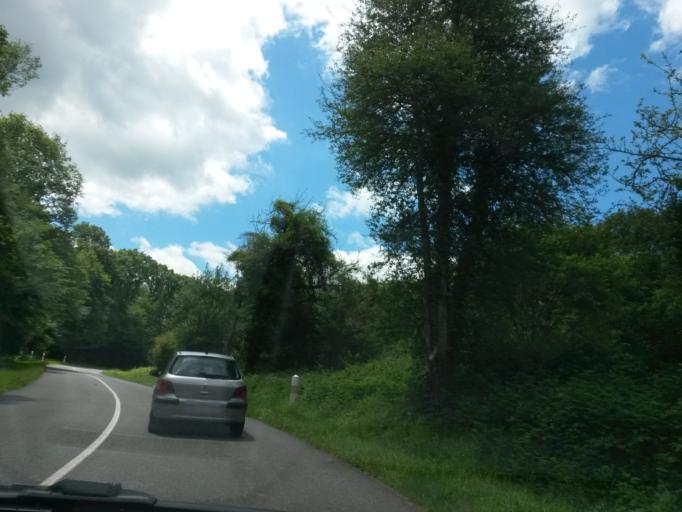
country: FR
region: Bourgogne
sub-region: Departement de la Nievre
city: Premery
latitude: 47.1809
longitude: 3.3153
